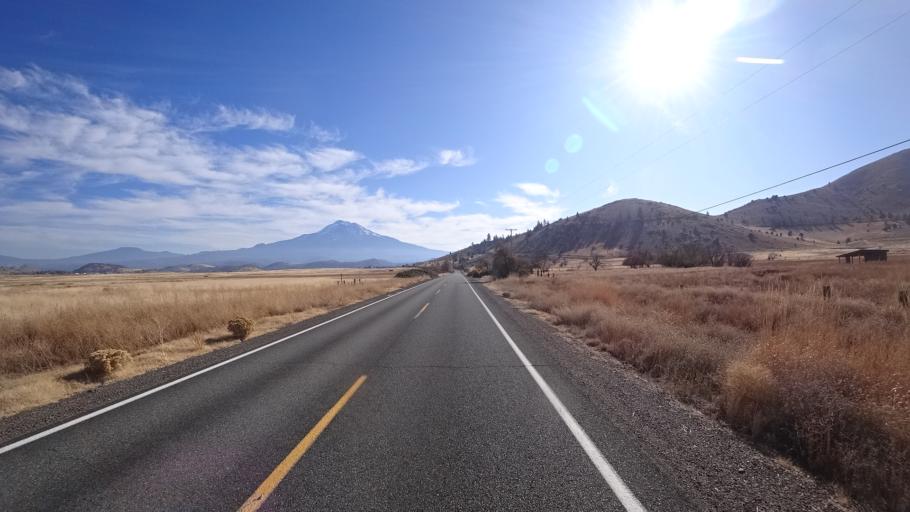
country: US
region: California
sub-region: Siskiyou County
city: Weed
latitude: 41.4712
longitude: -122.4772
